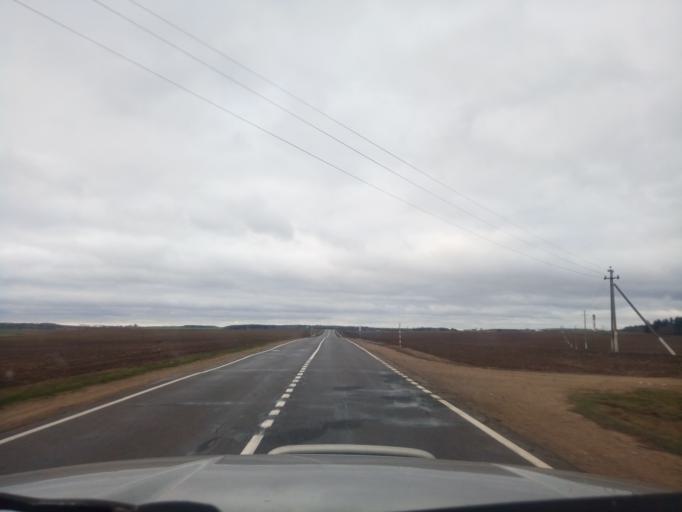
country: BY
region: Minsk
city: Kapyl'
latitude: 53.1999
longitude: 27.2101
